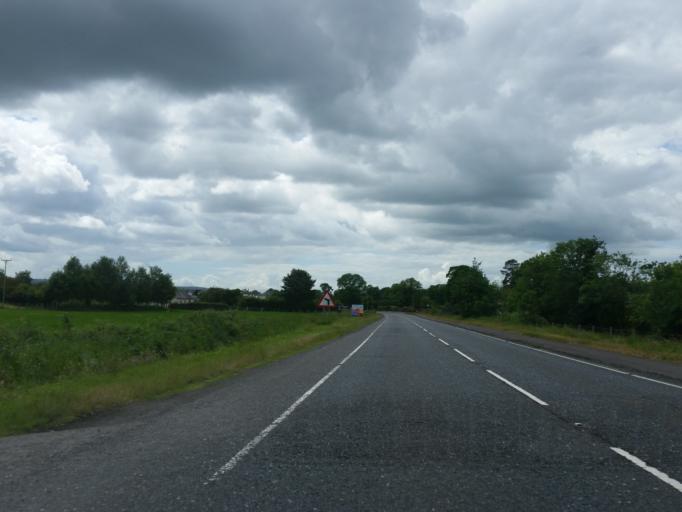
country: GB
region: Northern Ireland
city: Fivemiletown
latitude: 54.4344
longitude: -7.1241
